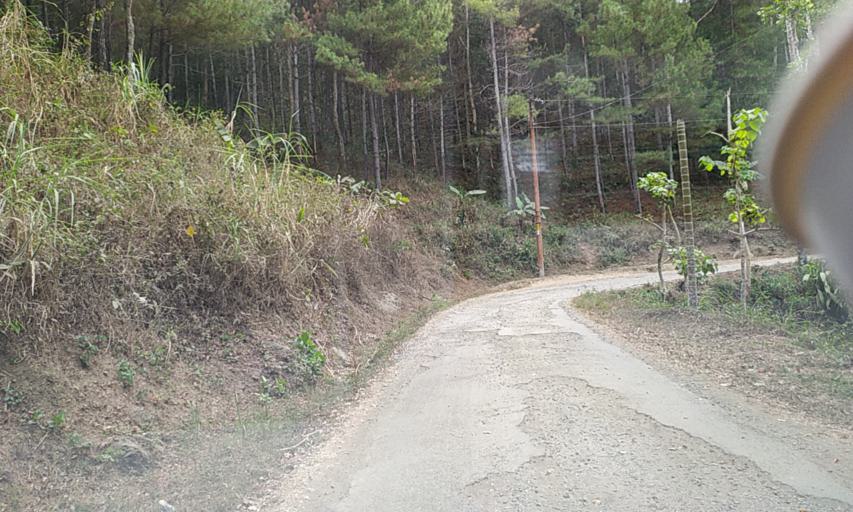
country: ID
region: Central Java
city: Bantarmangu
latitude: -7.3430
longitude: 108.9149
